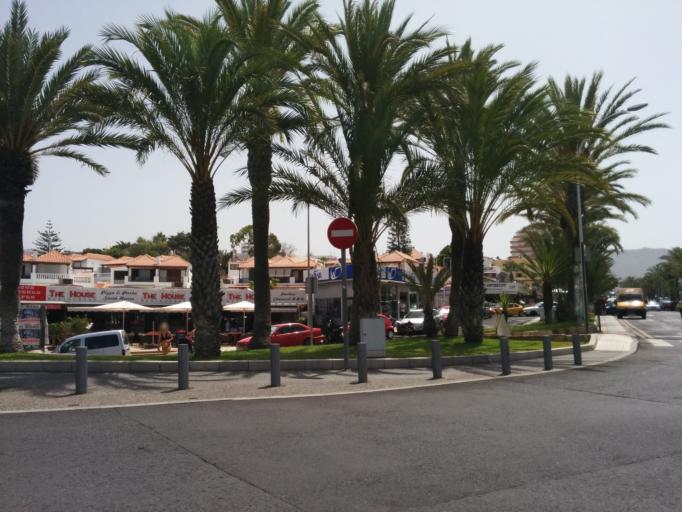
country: ES
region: Canary Islands
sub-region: Provincia de Santa Cruz de Tenerife
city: Playa de las Americas
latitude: 28.0625
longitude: -16.7310
